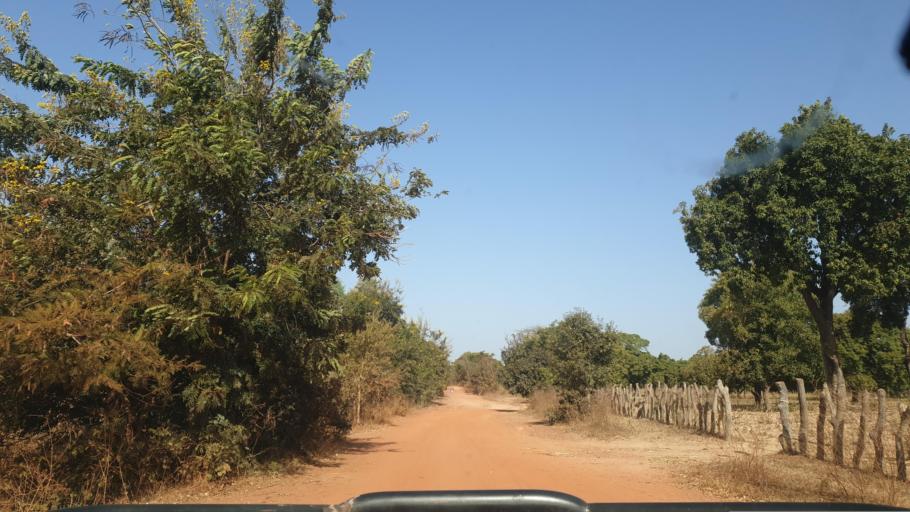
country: ML
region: Sikasso
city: Bougouni
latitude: 11.7735
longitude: -6.9038
